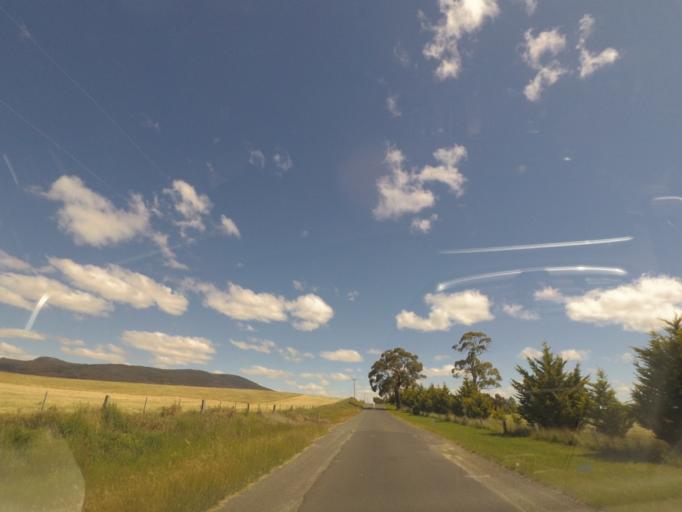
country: AU
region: Victoria
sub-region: Hume
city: Sunbury
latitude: -37.3298
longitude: 144.5592
